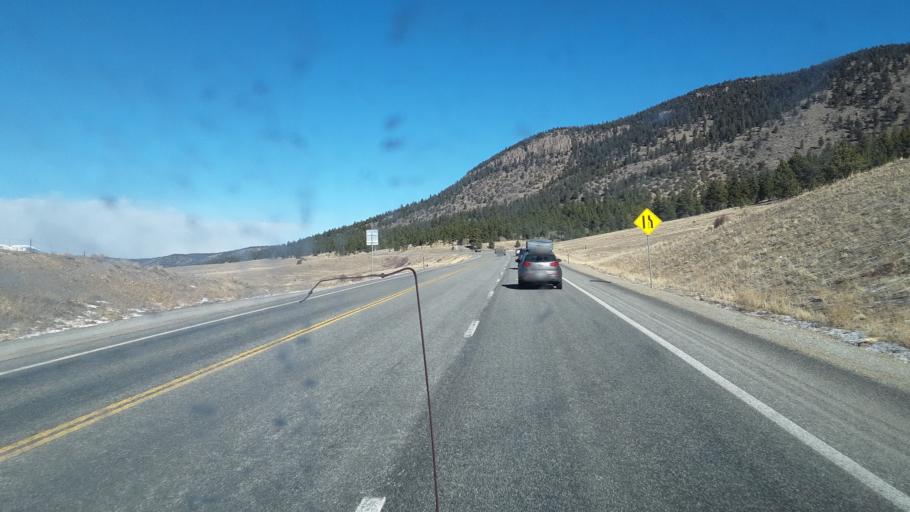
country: US
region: Colorado
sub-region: Chaffee County
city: Buena Vista
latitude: 38.8708
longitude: -105.9842
